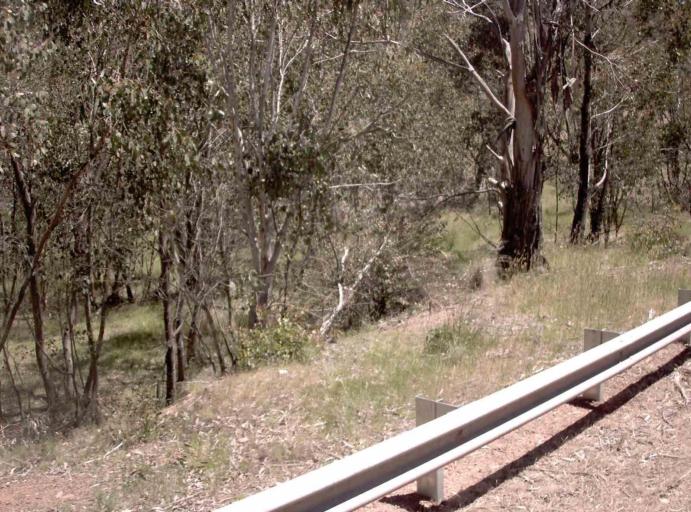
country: AU
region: New South Wales
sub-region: Snowy River
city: Jindabyne
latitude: -37.0668
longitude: 148.2612
